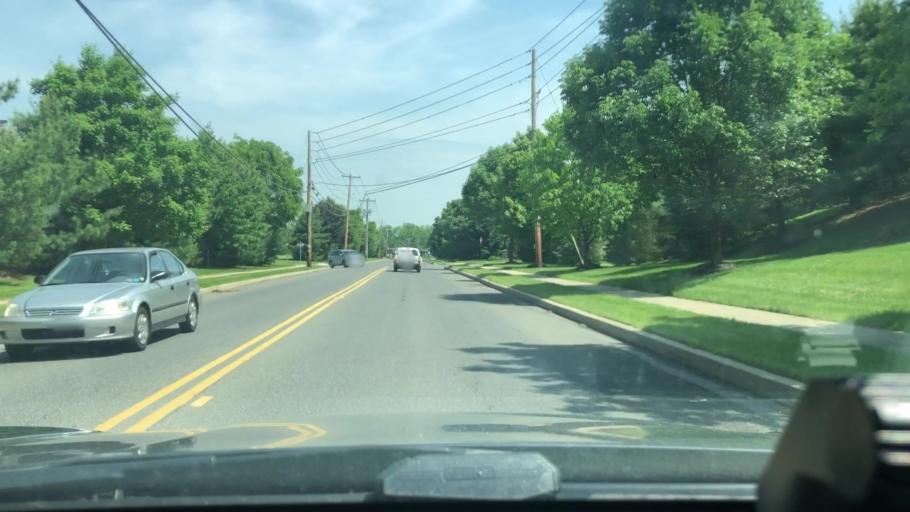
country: US
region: Pennsylvania
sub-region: Northampton County
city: Bethlehem
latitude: 40.6567
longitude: -75.3976
